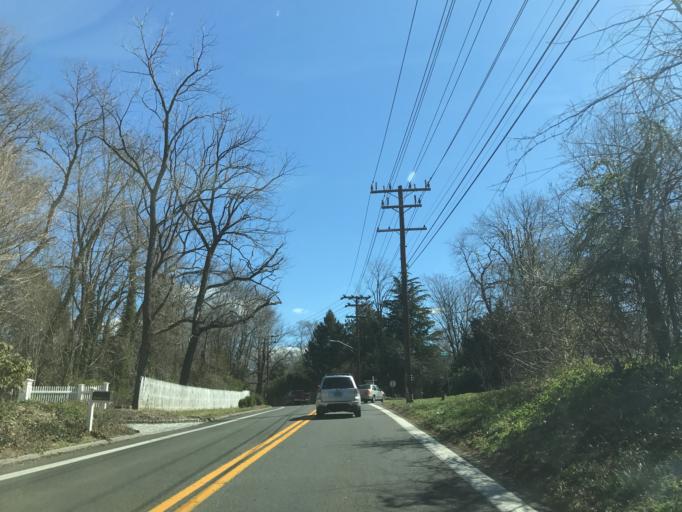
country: US
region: Maryland
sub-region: Anne Arundel County
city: Naval Academy
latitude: 38.9946
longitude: -76.4801
